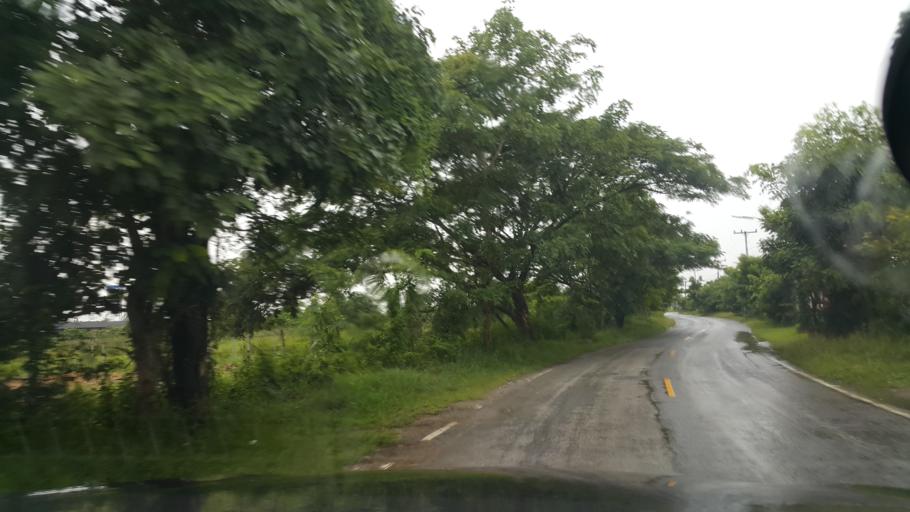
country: TH
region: Lamphun
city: Ban Thi
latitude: 18.6344
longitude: 99.1065
